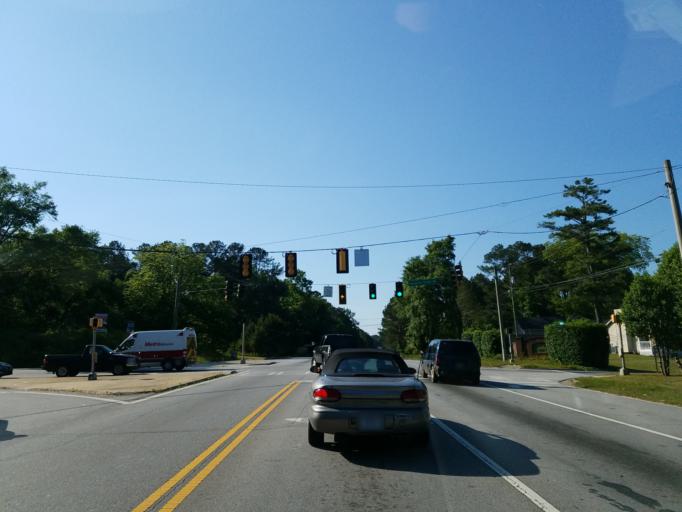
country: US
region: Georgia
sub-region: Paulding County
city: Dallas
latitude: 33.9177
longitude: -84.8280
